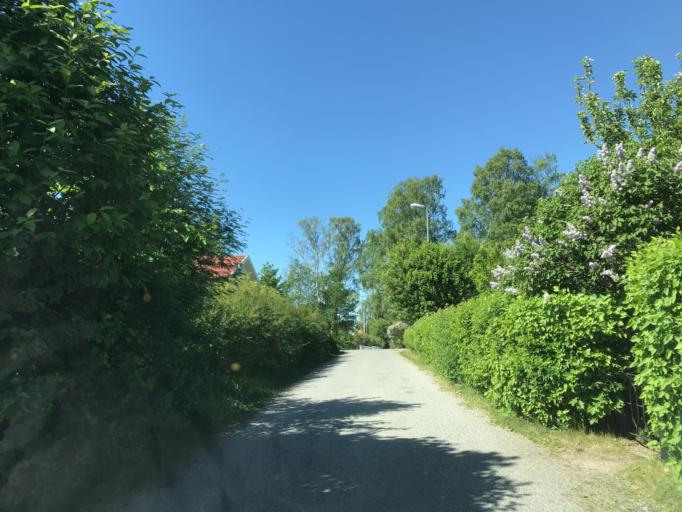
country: SE
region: Stockholm
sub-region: Sollentuna Kommun
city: Sollentuna
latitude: 59.4197
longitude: 17.9639
